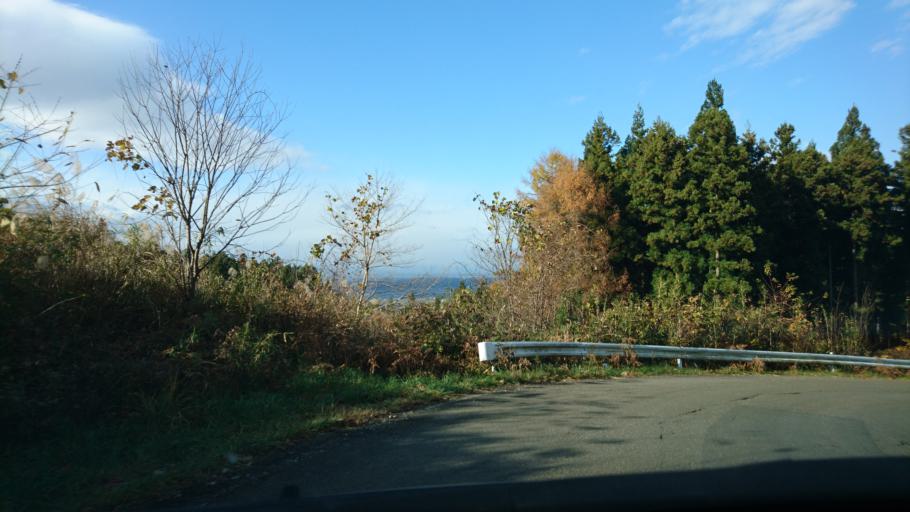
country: JP
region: Iwate
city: Ichinoseki
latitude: 39.0250
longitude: 141.1690
